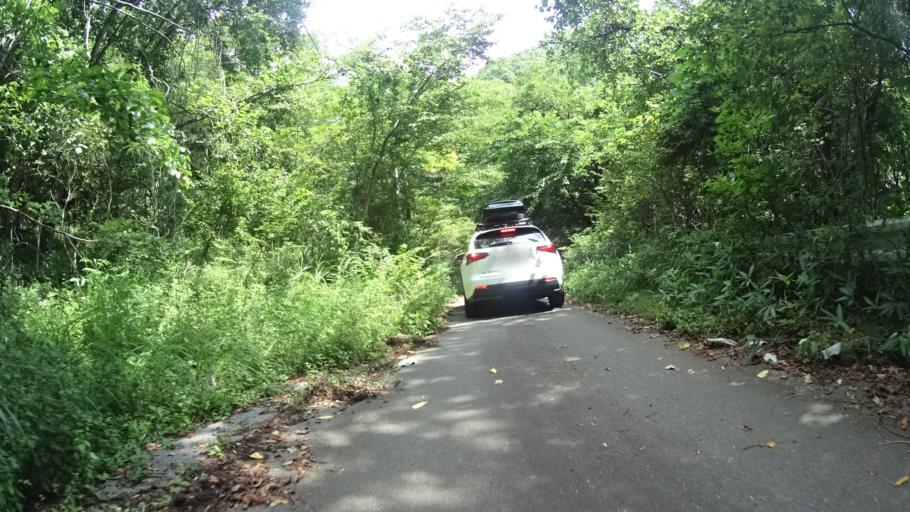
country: JP
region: Yamanashi
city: Nirasaki
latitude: 35.8822
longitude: 138.5031
